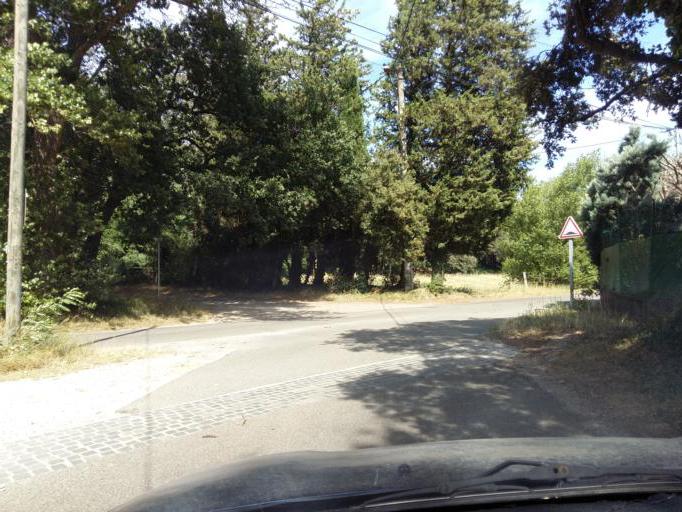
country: FR
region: Provence-Alpes-Cote d'Azur
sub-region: Departement du Vaucluse
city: Piolenc
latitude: 44.1870
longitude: 4.7547
